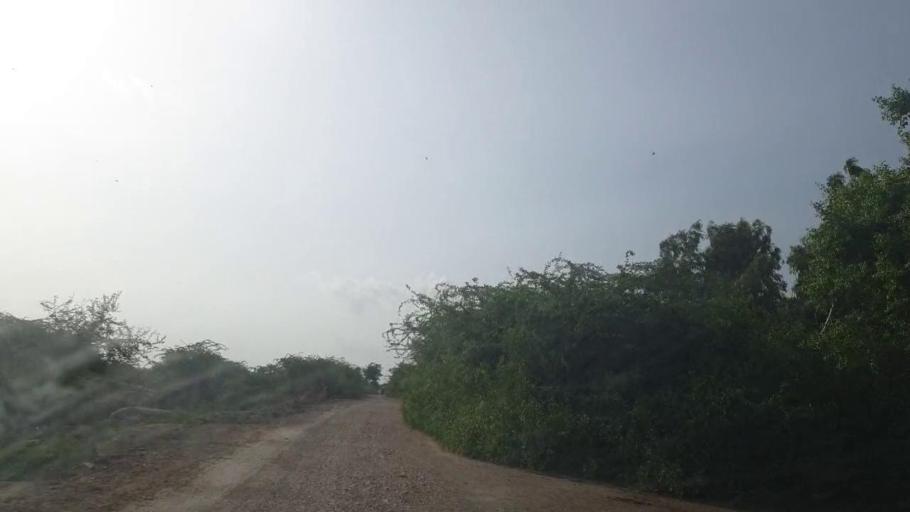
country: PK
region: Sindh
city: Tando Bago
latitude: 24.7582
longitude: 69.0832
